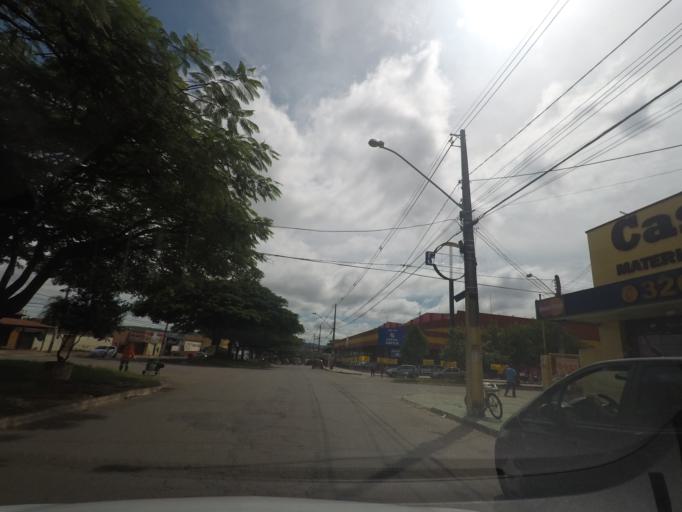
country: BR
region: Goias
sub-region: Goiania
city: Goiania
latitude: -16.6637
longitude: -49.2140
